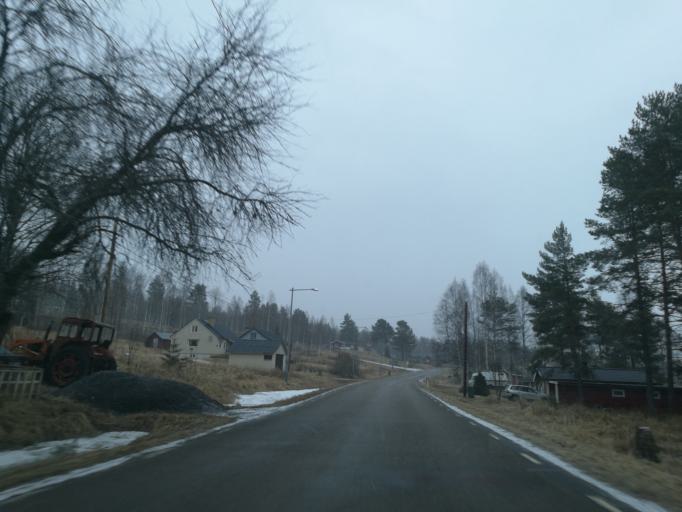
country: NO
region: Hedmark
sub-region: Asnes
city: Flisa
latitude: 60.6951
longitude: 12.4768
